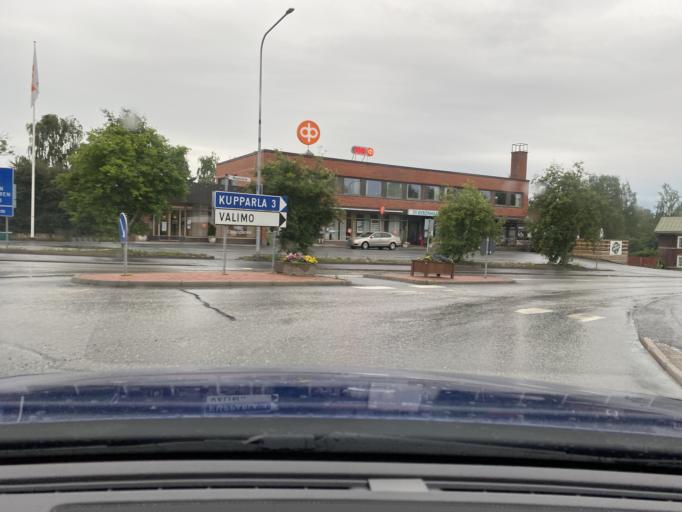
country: FI
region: Ostrobothnia
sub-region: Kyroenmaa
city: Laihia
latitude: 62.9762
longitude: 22.0113
